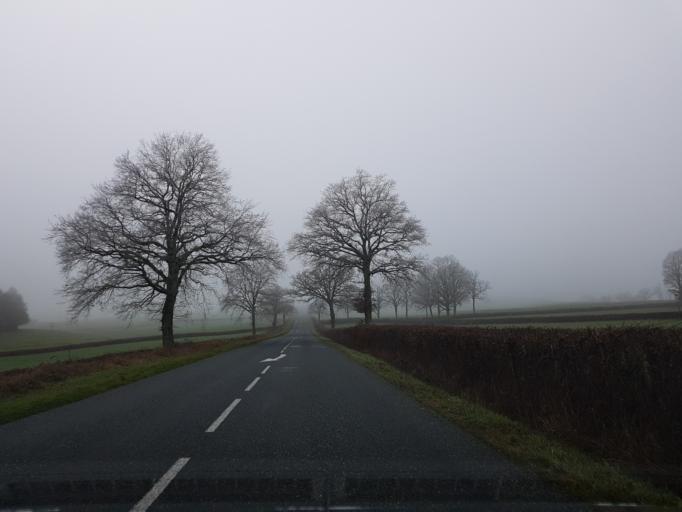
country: FR
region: Bourgogne
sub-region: Departement de Saone-et-Loire
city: Saint-Berain-sous-Sanvignes
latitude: 46.7062
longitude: 4.2300
